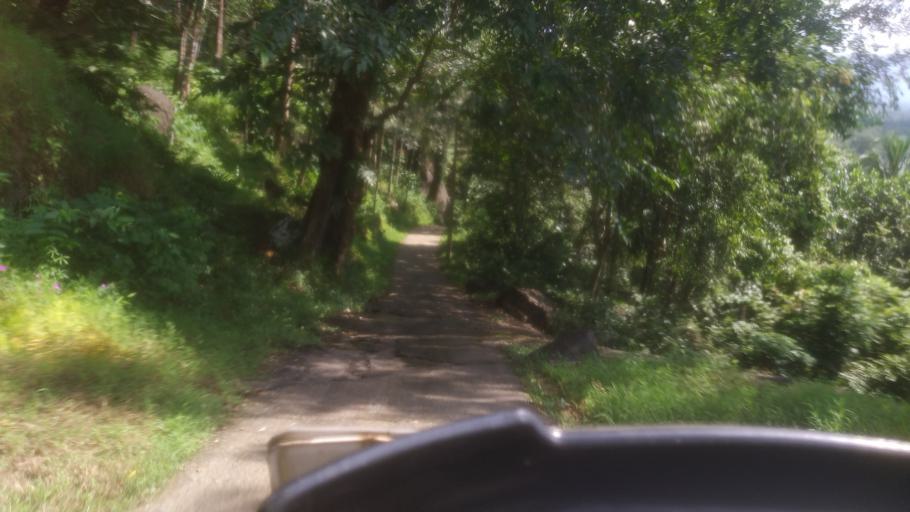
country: IN
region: Kerala
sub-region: Idukki
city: Idukki
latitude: 9.9628
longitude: 76.8247
